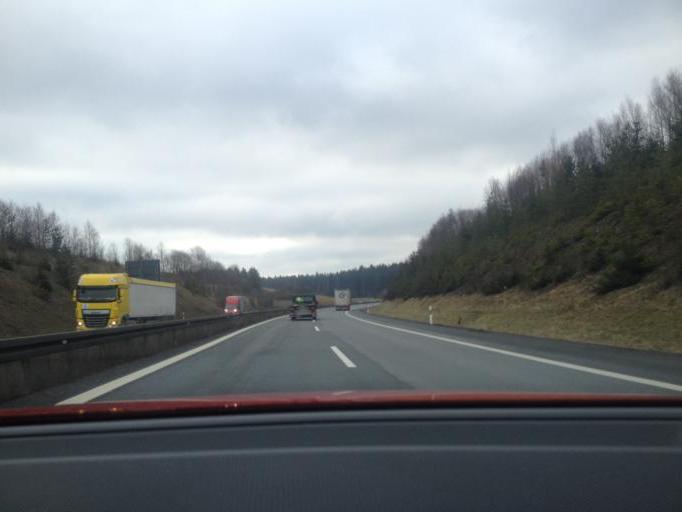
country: DE
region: Bavaria
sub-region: Upper Franconia
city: Schonwald
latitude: 50.2138
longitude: 12.1010
